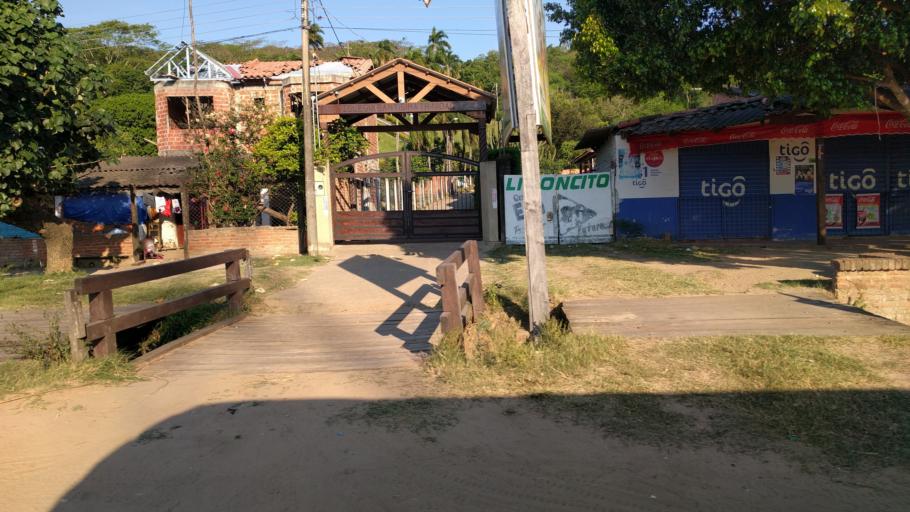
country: BO
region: Santa Cruz
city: Limoncito
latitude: -18.0306
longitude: -63.4037
